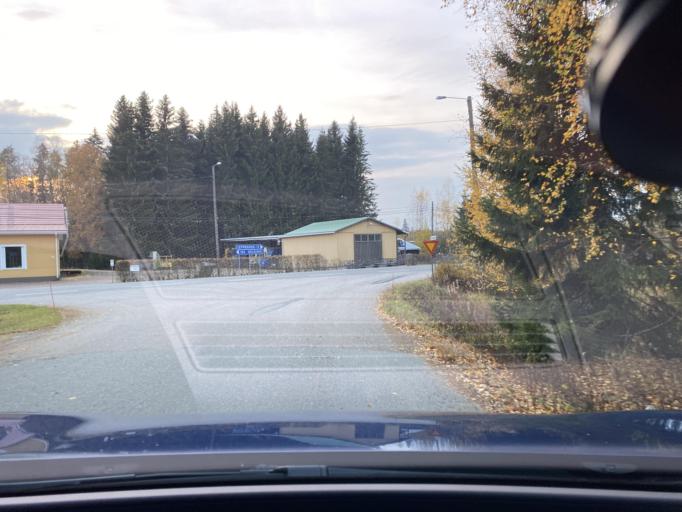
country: FI
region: Varsinais-Suomi
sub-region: Loimaa
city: Alastaro
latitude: 61.0853
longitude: 22.9180
